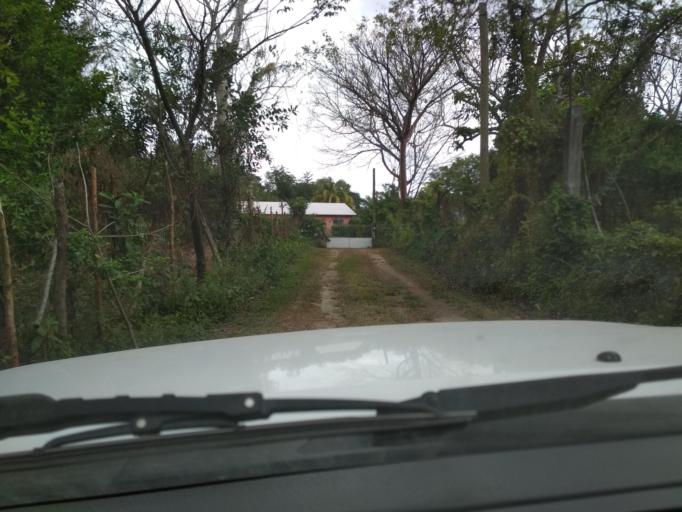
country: MX
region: Veracruz
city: El Tejar
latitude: 19.0632
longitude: -96.1554
